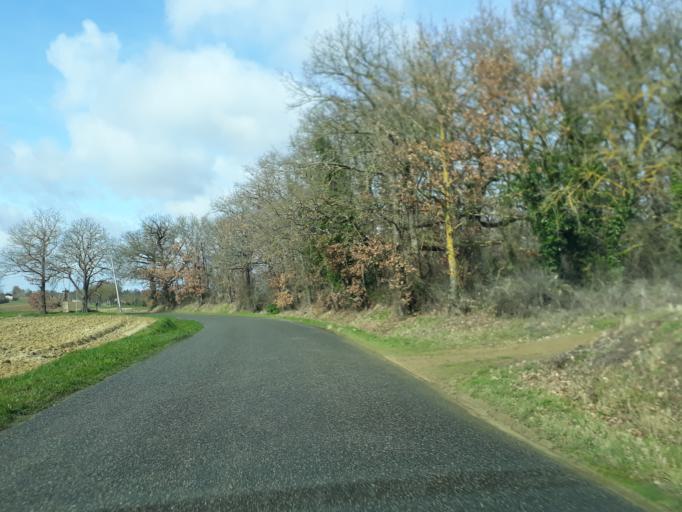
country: FR
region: Midi-Pyrenees
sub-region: Departement du Gers
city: Pujaudran
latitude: 43.6272
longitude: 1.0217
